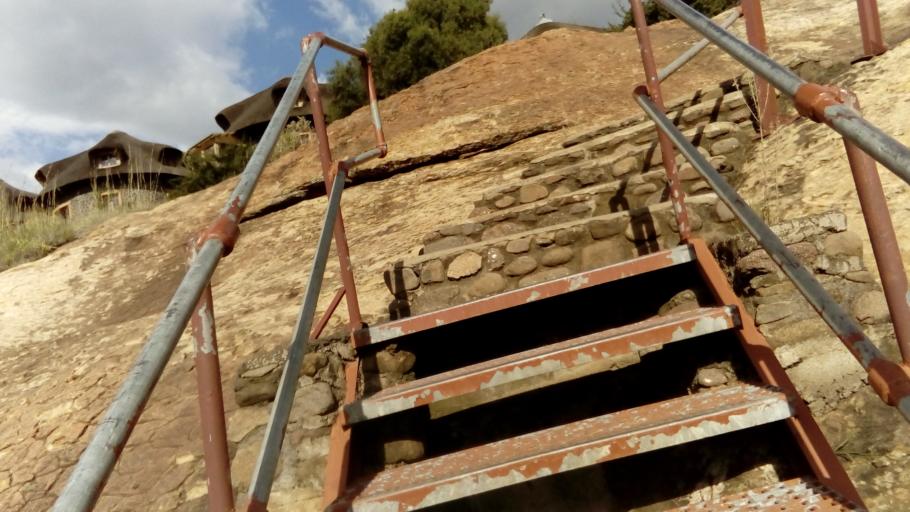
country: LS
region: Butha-Buthe
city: Butha-Buthe
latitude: -28.7532
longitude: 28.4947
